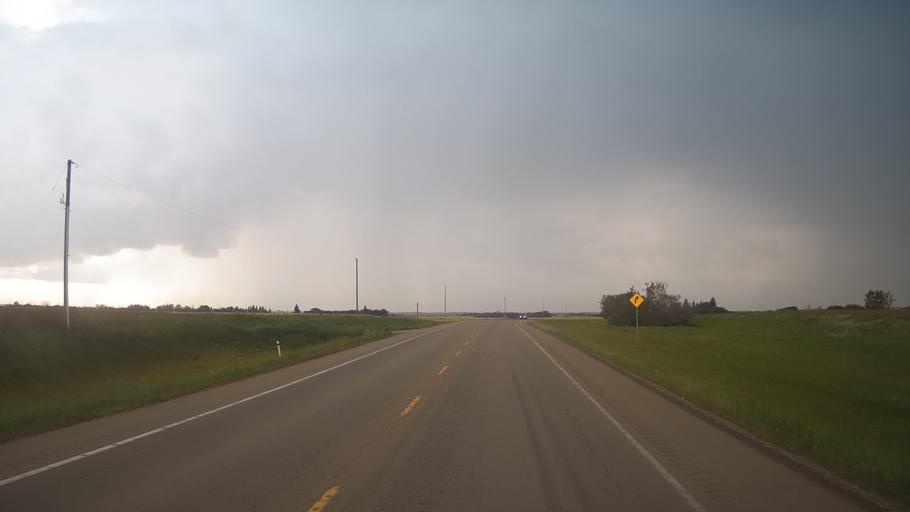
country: CA
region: Alberta
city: Tofield
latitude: 53.3226
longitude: -112.5494
